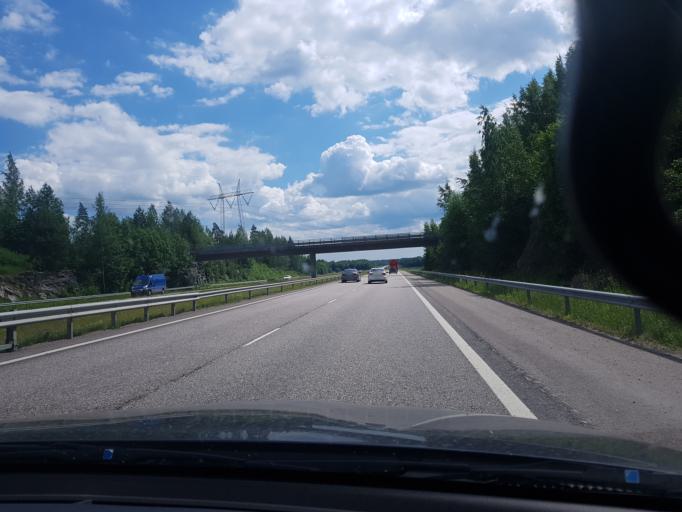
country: FI
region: Uusimaa
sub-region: Helsinki
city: Nurmijaervi
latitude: 60.5439
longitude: 24.8381
